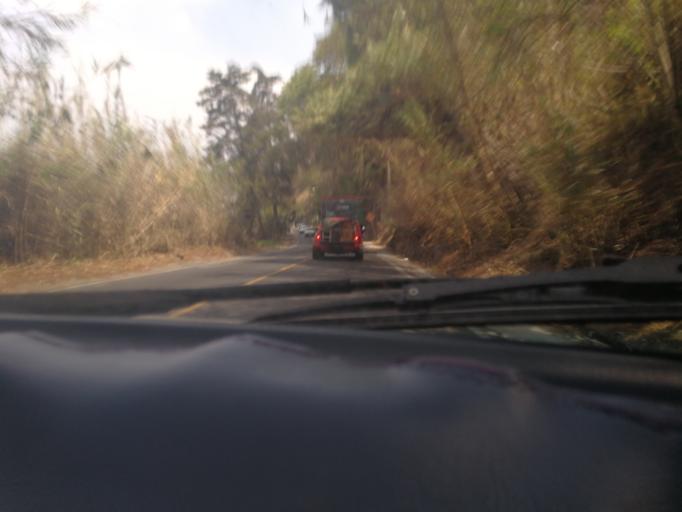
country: GT
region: Guatemala
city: Guatemala City
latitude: 14.6187
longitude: -90.4758
